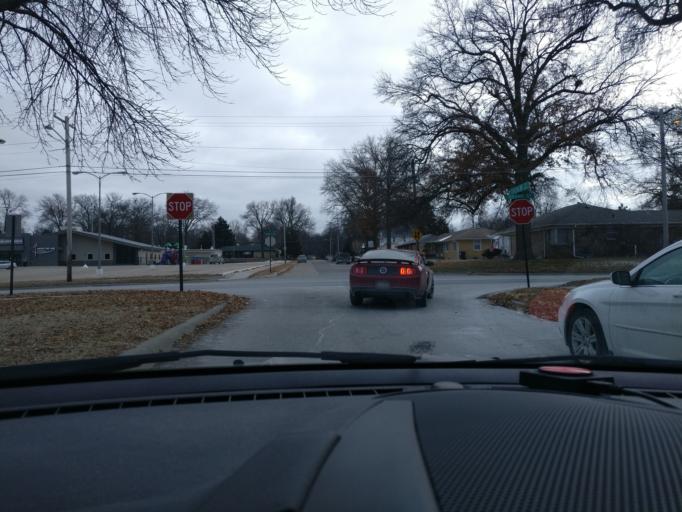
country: US
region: Nebraska
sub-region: Lancaster County
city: Lincoln
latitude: 40.8428
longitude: -96.6402
